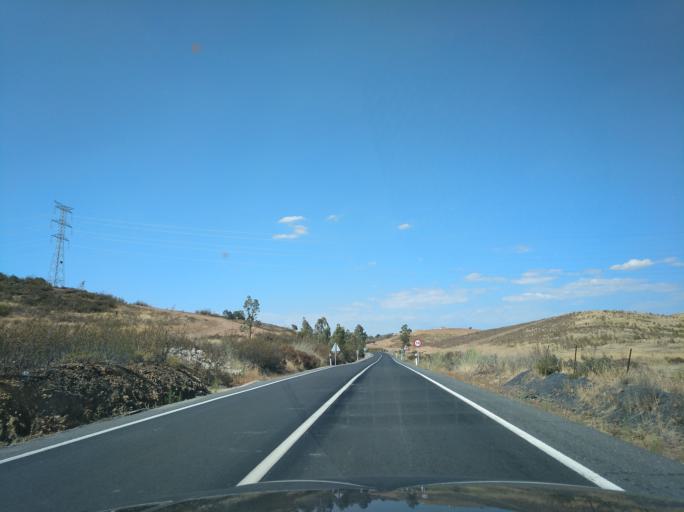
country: ES
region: Andalusia
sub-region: Provincia de Huelva
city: Alosno
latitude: 37.5109
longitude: -7.1325
